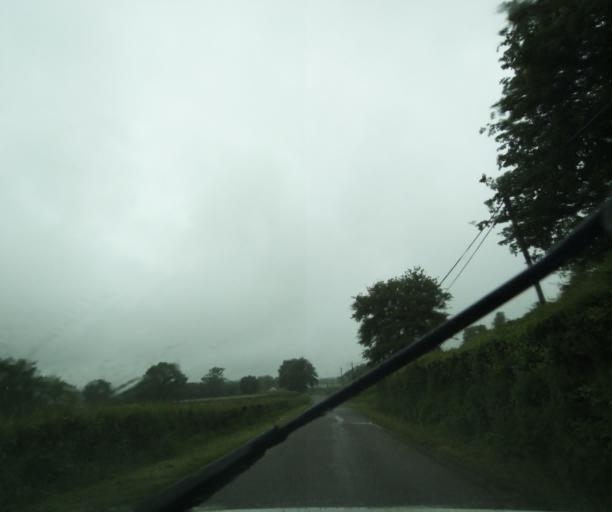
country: FR
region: Bourgogne
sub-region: Departement de Saone-et-Loire
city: Charolles
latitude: 46.4305
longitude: 4.3440
